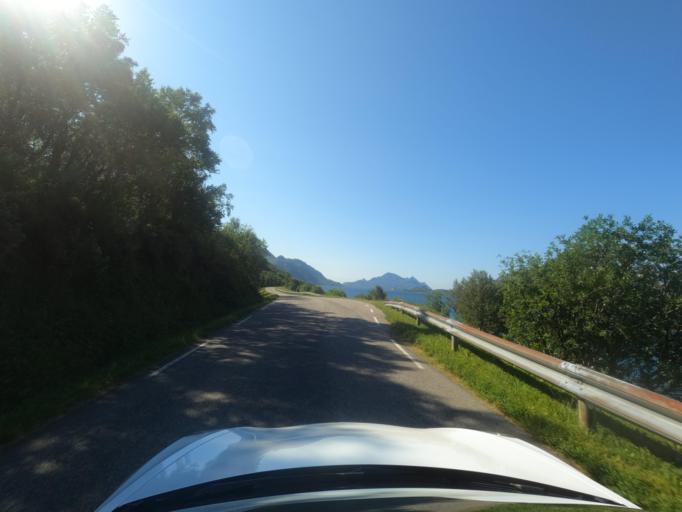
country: NO
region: Nordland
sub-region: Hadsel
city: Stokmarknes
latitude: 68.3741
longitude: 15.0773
